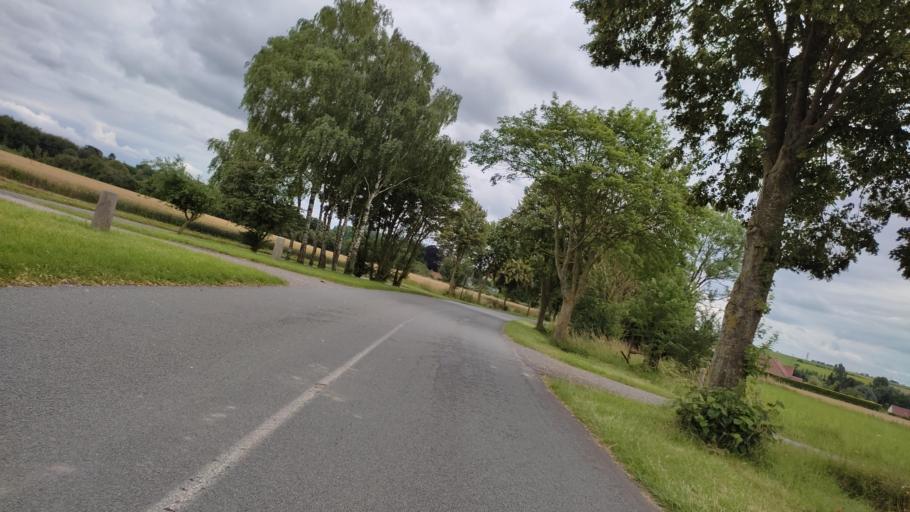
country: FR
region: Nord-Pas-de-Calais
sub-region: Departement du Pas-de-Calais
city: Riviere
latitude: 50.2359
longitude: 2.6801
